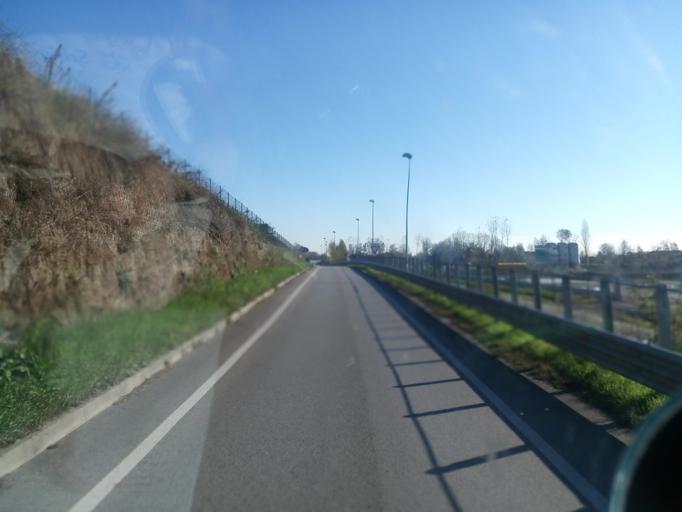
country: IT
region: Veneto
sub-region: Provincia di Padova
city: Loreggia
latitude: 45.6140
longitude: 11.9485
